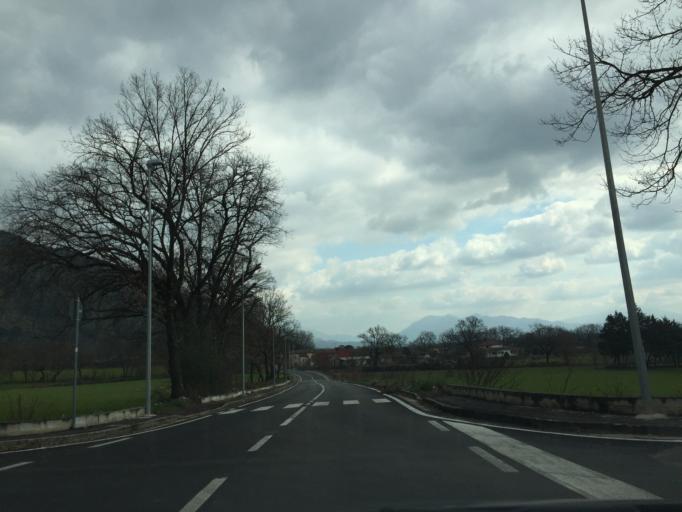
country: IT
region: Latium
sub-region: Provincia di Frosinone
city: Villa Santa Lucia
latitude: 41.4963
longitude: 13.7684
